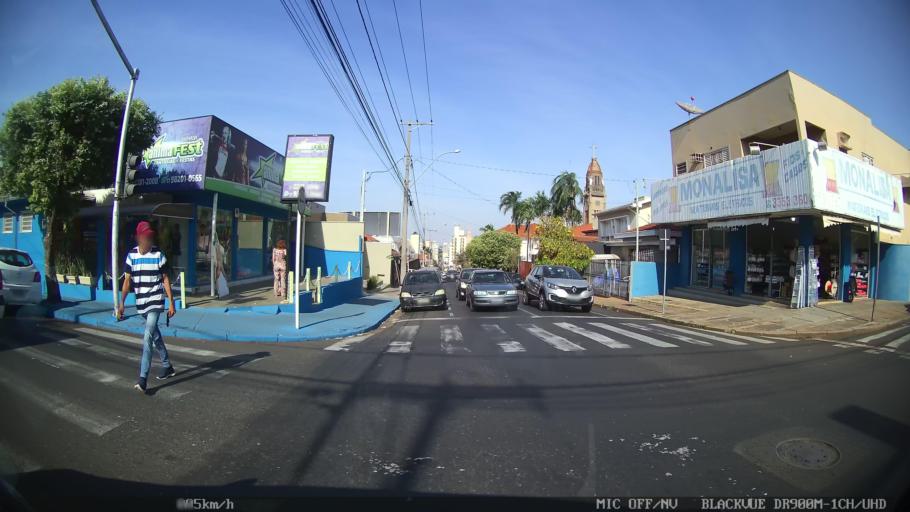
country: BR
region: Sao Paulo
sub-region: Sao Jose Do Rio Preto
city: Sao Jose do Rio Preto
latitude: -20.8057
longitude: -49.3882
